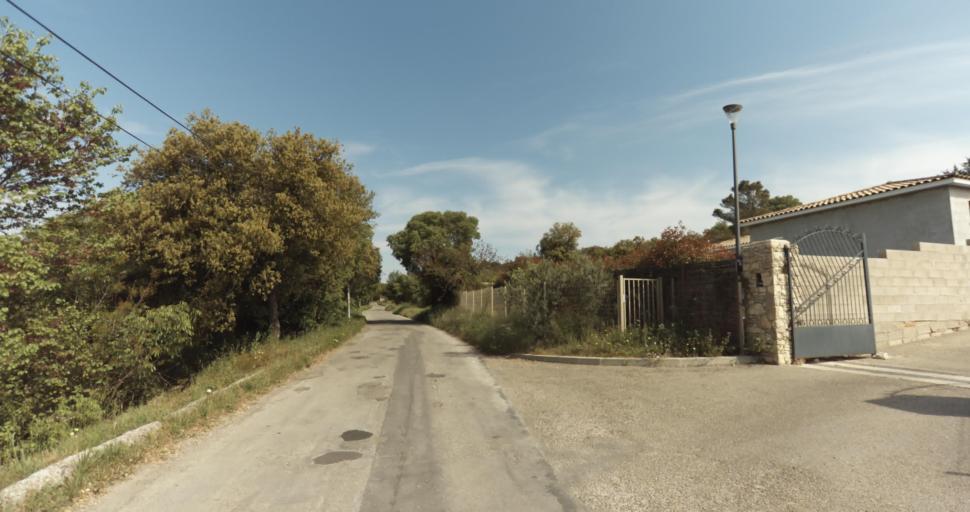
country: FR
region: Languedoc-Roussillon
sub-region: Departement du Gard
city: Rodilhan
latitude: 43.8596
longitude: 4.3948
